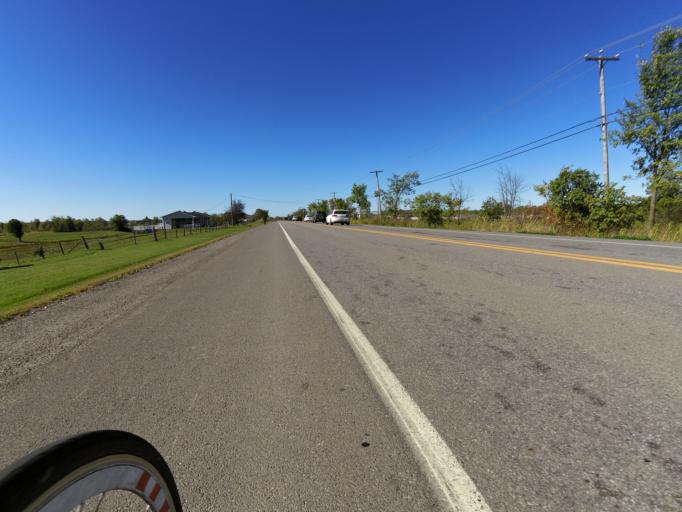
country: CA
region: Quebec
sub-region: Outaouais
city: Gatineau
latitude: 45.5138
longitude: -75.5295
